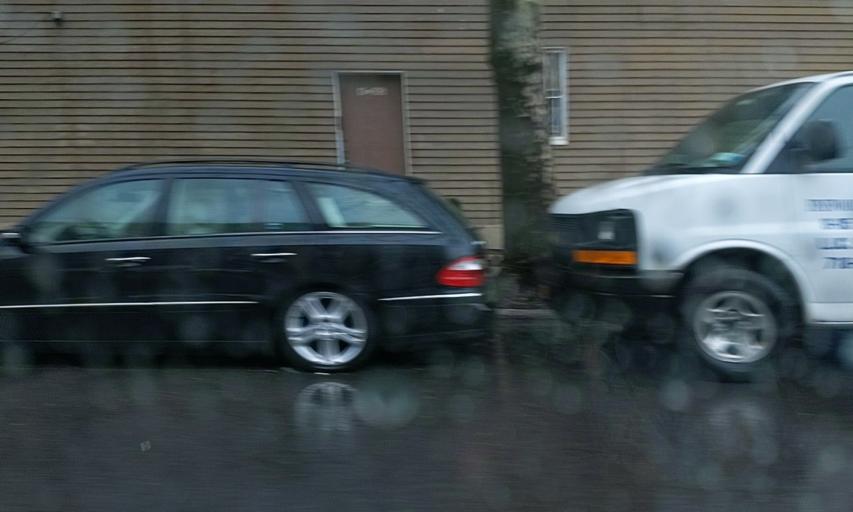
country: US
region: New York
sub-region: Queens County
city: Long Island City
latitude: 40.7619
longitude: -73.9421
